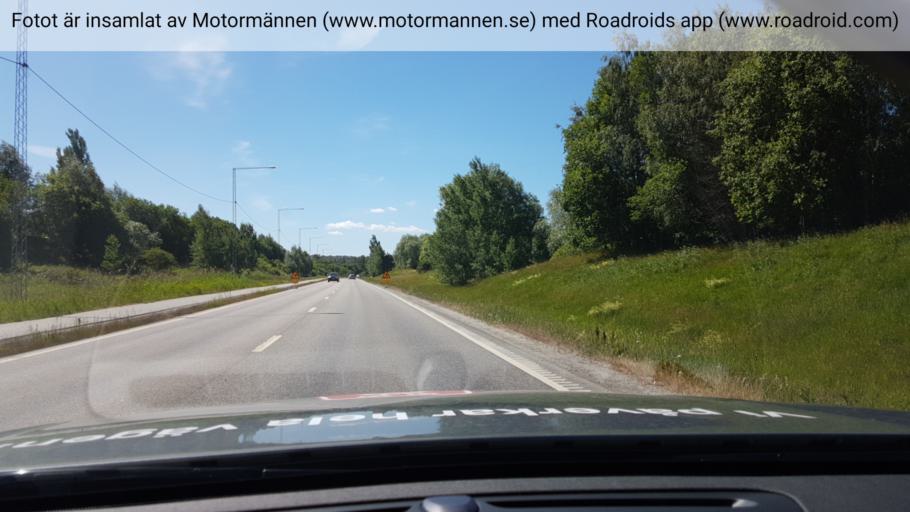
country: SE
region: Stockholm
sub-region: Haninge Kommun
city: Haninge
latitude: 59.1874
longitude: 18.1731
